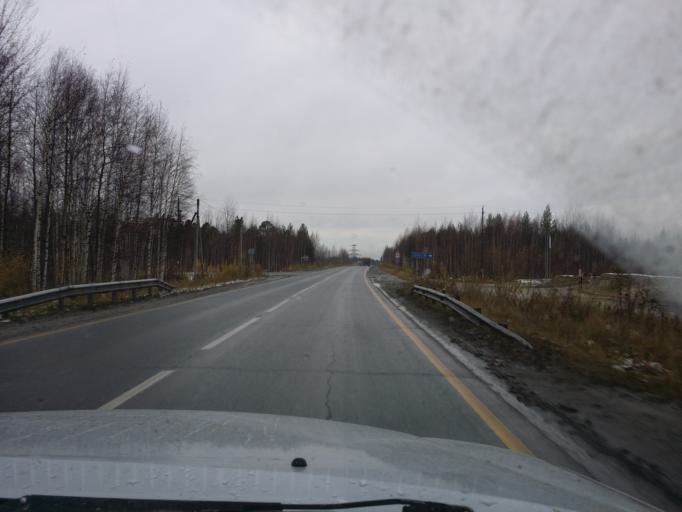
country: RU
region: Khanty-Mansiyskiy Avtonomnyy Okrug
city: Megion
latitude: 61.1022
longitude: 75.9880
